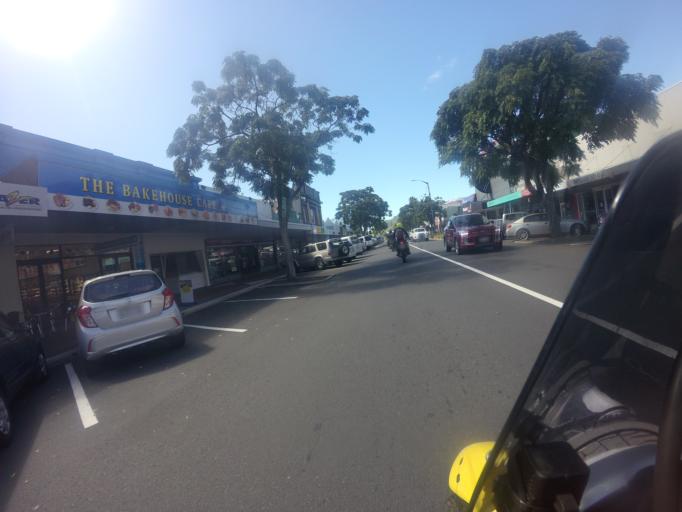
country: NZ
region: Bay of Plenty
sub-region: Whakatane District
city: Whakatane
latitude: -37.9510
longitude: 176.9970
